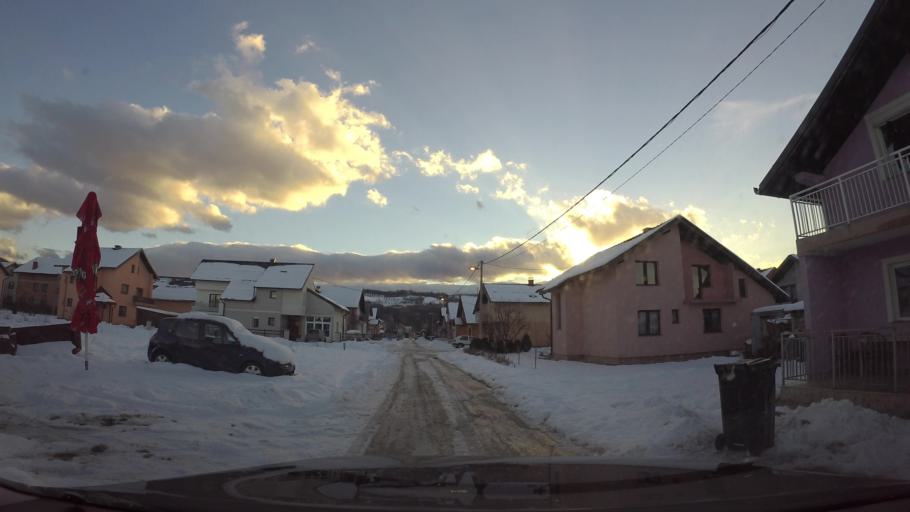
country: BA
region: Federation of Bosnia and Herzegovina
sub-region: Kanton Sarajevo
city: Sarajevo
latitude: 43.8130
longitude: 18.3617
